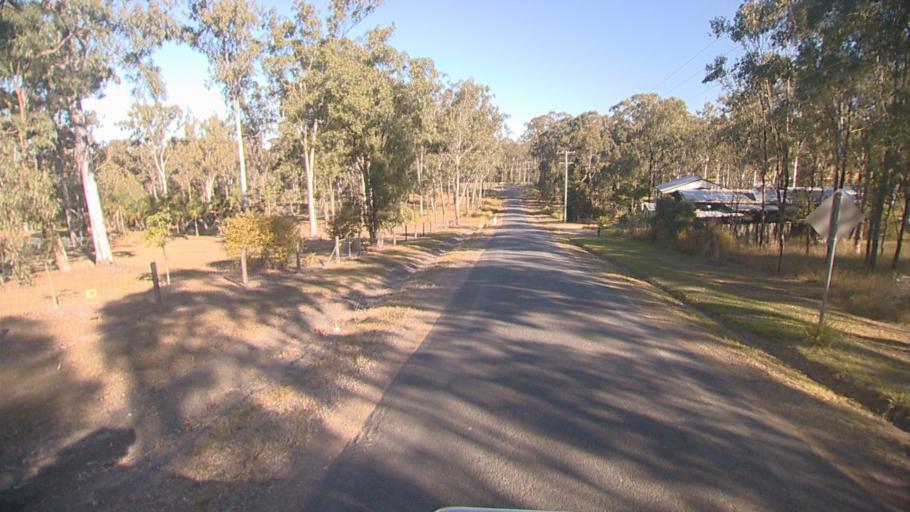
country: AU
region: Queensland
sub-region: Logan
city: North Maclean
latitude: -27.8088
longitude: 153.0335
